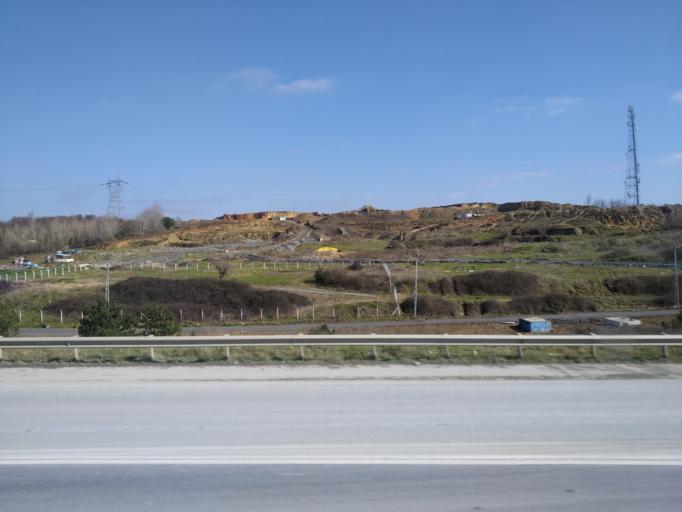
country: TR
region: Istanbul
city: Kemerburgaz
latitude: 41.1650
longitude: 28.8919
